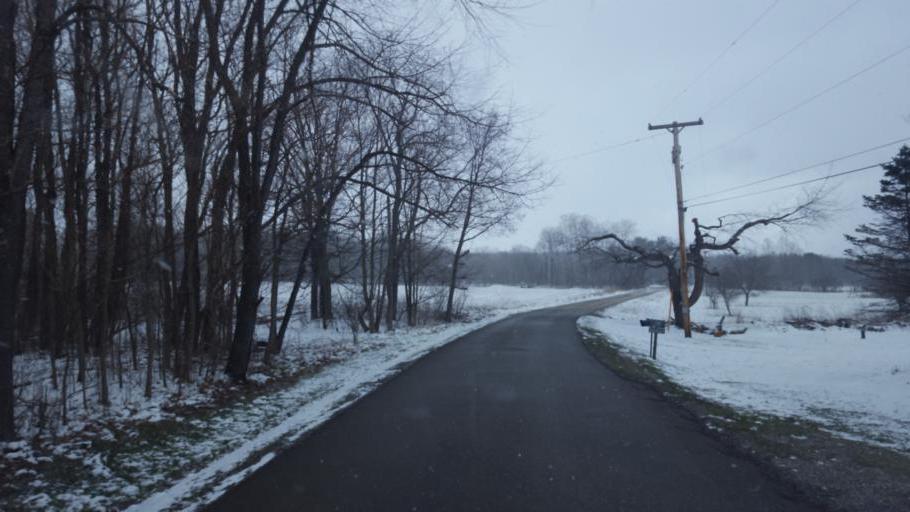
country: US
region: Pennsylvania
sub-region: Mercer County
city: Stoneboro
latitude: 41.4248
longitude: -80.0731
